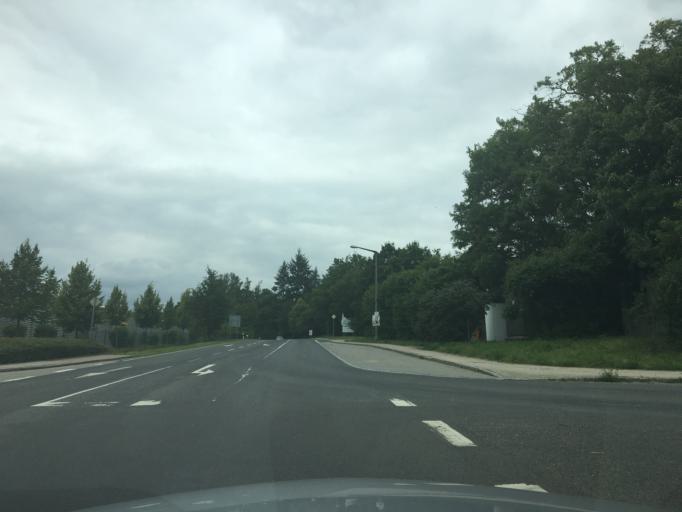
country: DE
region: Bavaria
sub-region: Regierungsbezirk Mittelfranken
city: Greding
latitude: 49.0431
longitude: 11.3629
